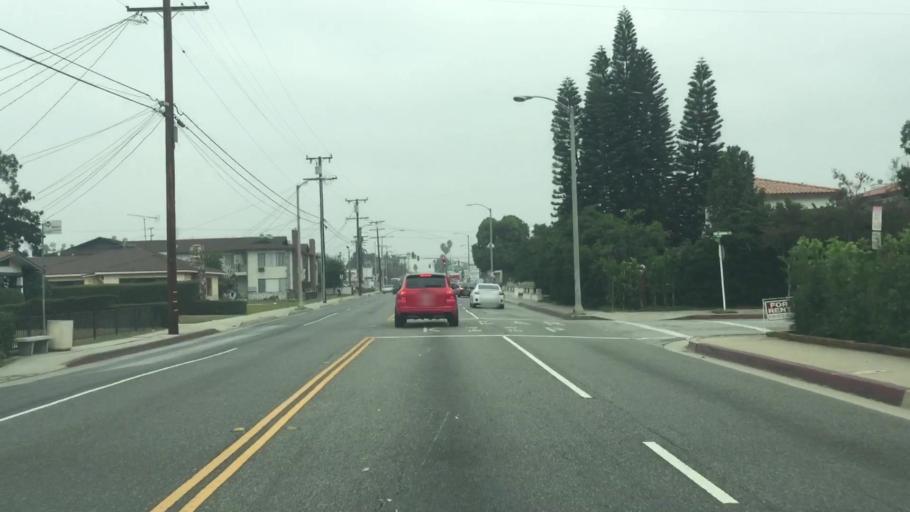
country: US
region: California
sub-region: Los Angeles County
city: Alhambra
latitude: 34.0826
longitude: -118.1345
